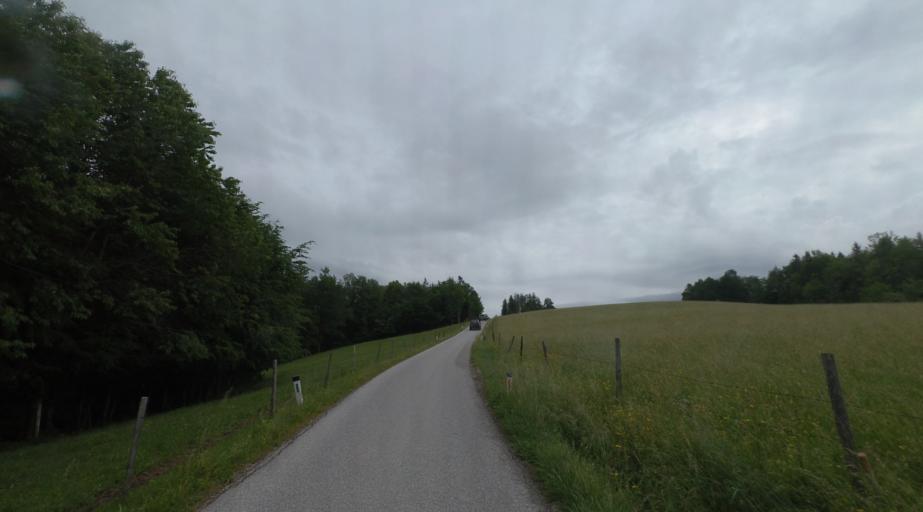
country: AT
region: Upper Austria
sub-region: Politischer Bezirk Kirchdorf an der Krems
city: Micheldorf in Oberoesterreich
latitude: 47.9002
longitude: 14.1571
